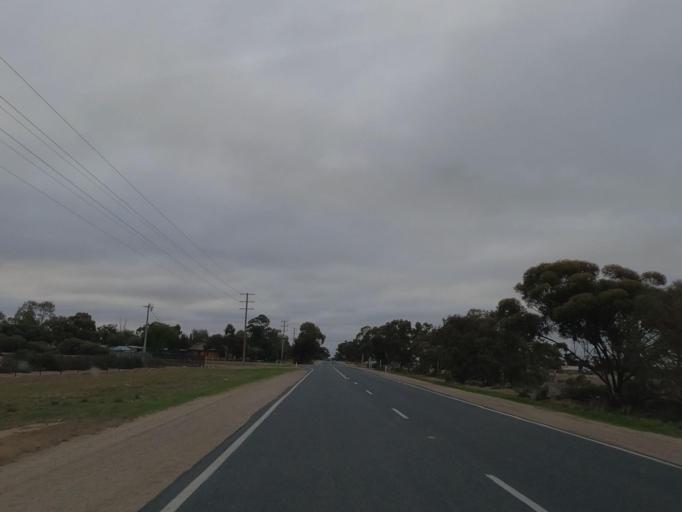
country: AU
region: Victoria
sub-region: Swan Hill
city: Swan Hill
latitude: -35.3867
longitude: 143.5677
